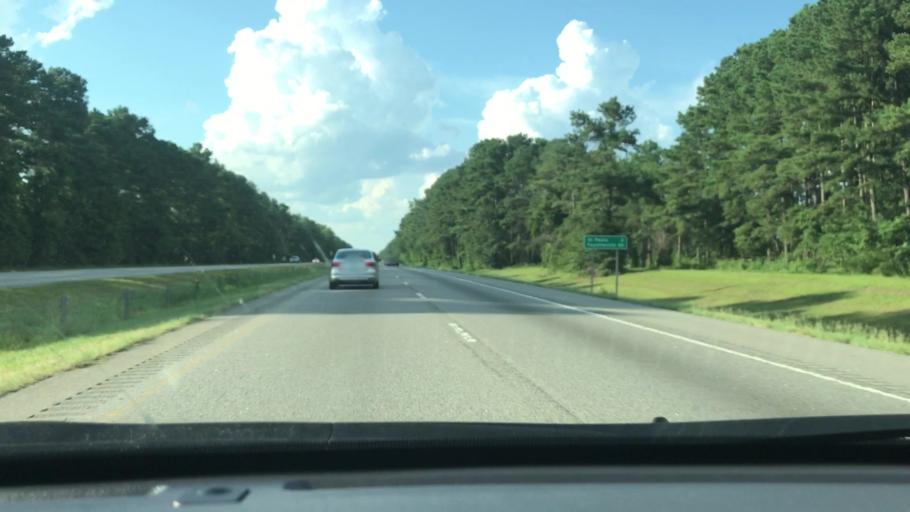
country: US
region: North Carolina
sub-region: Robeson County
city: Saint Pauls
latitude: 34.7322
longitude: -78.9972
